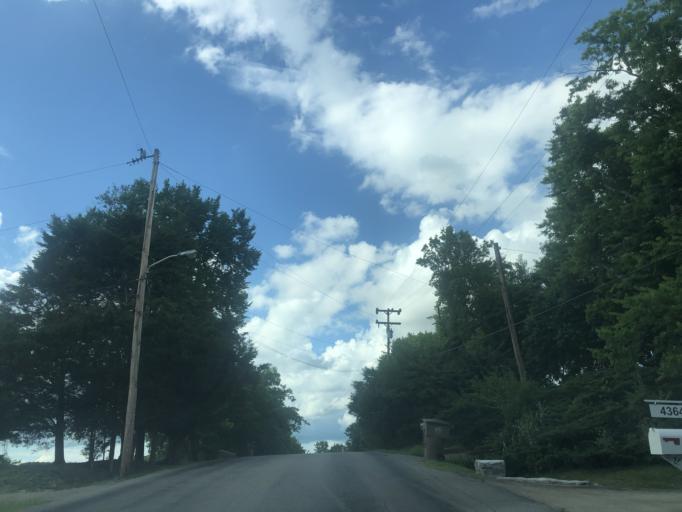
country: US
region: Tennessee
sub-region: Davidson County
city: Nashville
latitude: 36.2132
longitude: -86.8581
